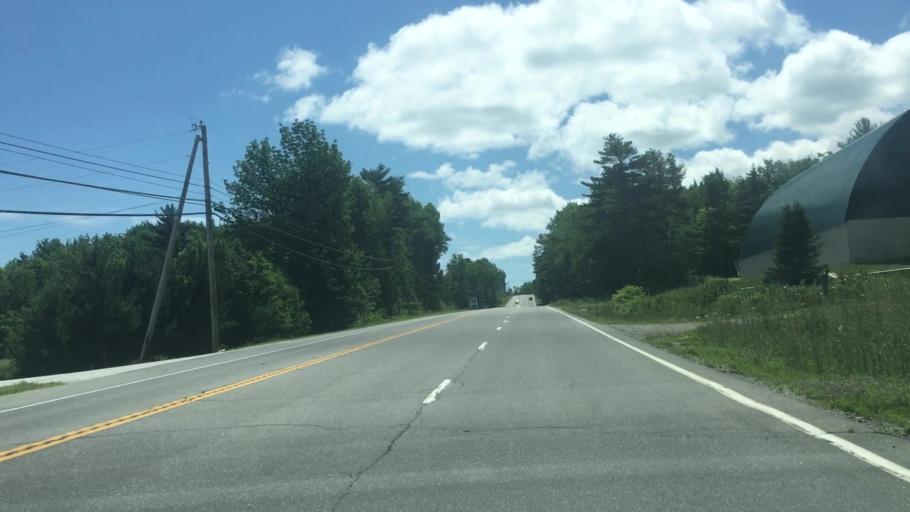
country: US
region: Maine
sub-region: Waldo County
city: Northport
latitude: 44.3675
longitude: -68.9803
